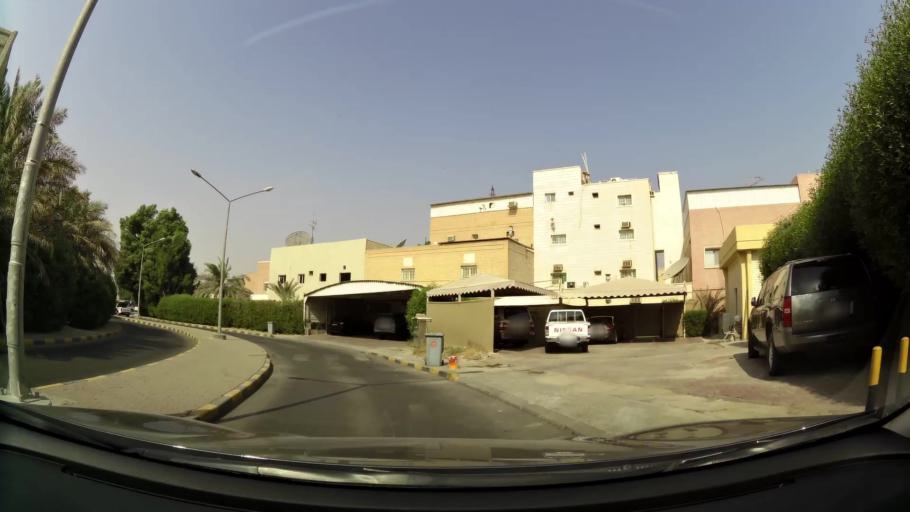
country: KW
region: Al Asimah
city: Ar Rabiyah
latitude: 29.2878
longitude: 47.8926
